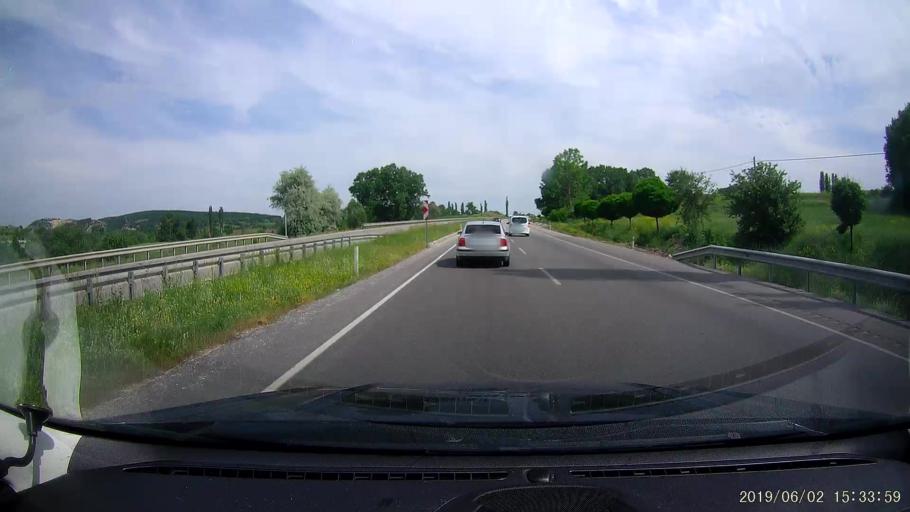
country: TR
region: Amasya
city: Saraycik
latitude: 40.9185
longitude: 35.1692
